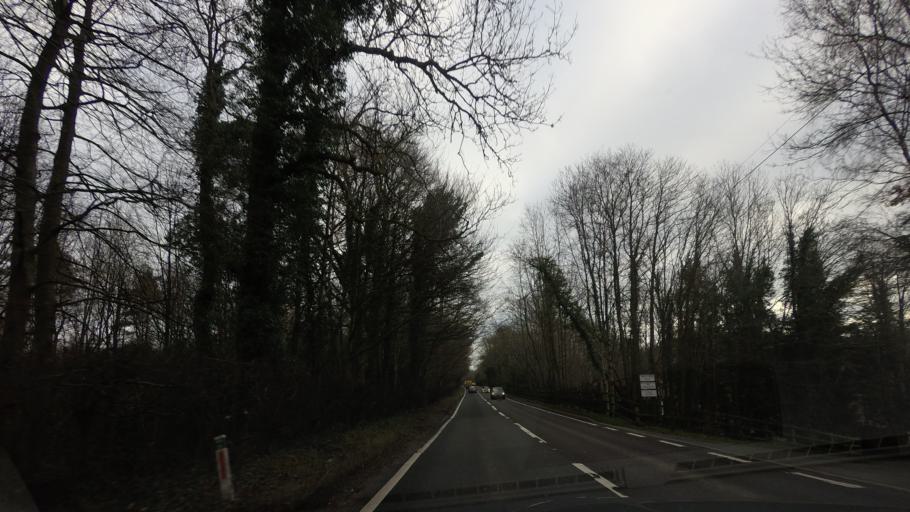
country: GB
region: England
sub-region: East Sussex
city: Wadhurst
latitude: 51.0863
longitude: 0.4074
